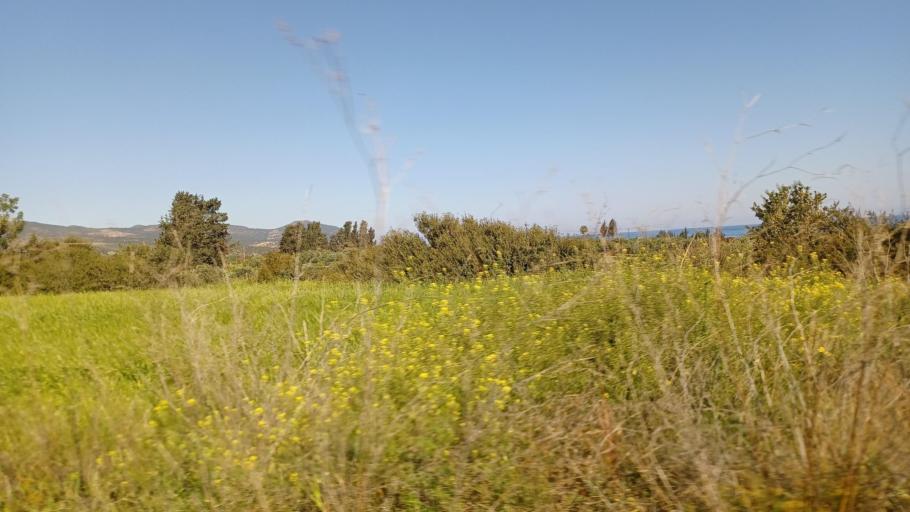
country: CY
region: Pafos
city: Polis
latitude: 35.0316
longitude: 32.3940
